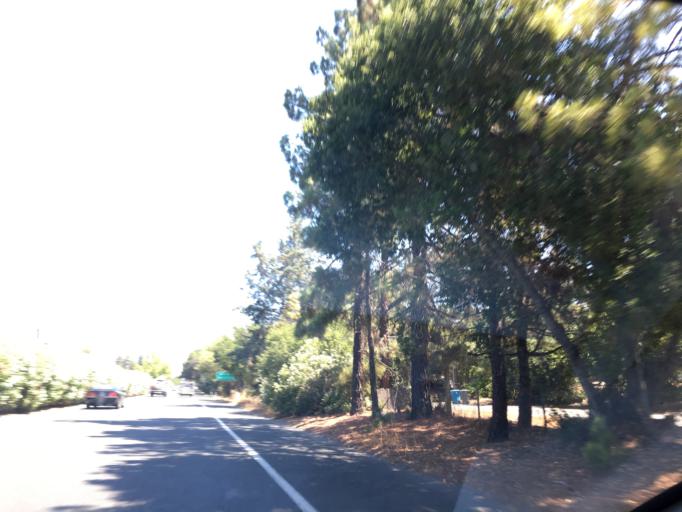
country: US
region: California
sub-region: Santa Clara County
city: Loyola
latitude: 37.3624
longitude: -122.1003
